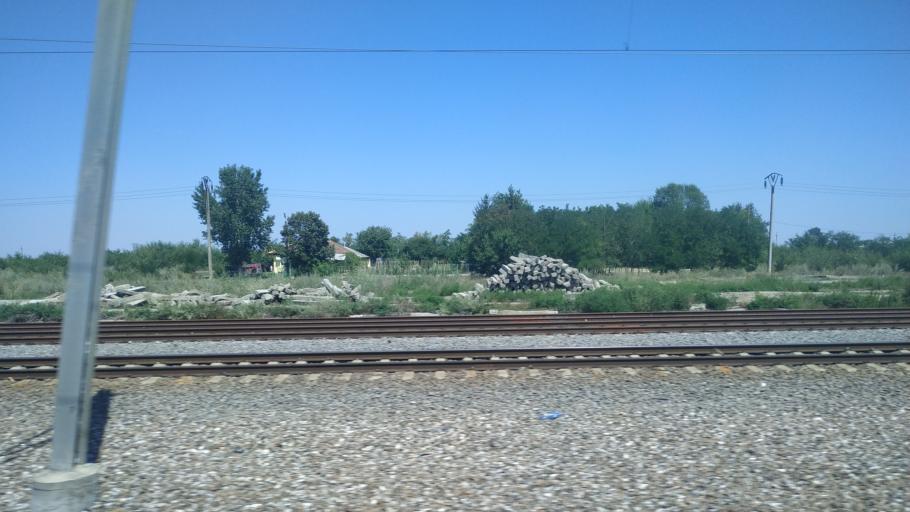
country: RO
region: Calarasi
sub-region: Comuna Borcea
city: Borcea
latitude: 44.4202
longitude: 27.6957
